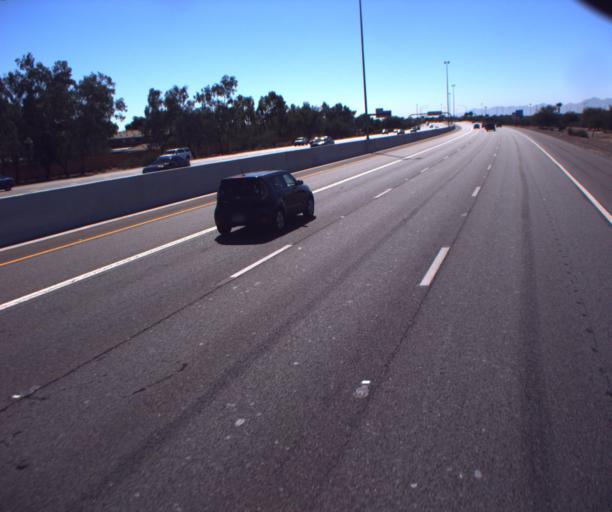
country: US
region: Arizona
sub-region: Maricopa County
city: Sun City
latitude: 33.6268
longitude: -112.2405
